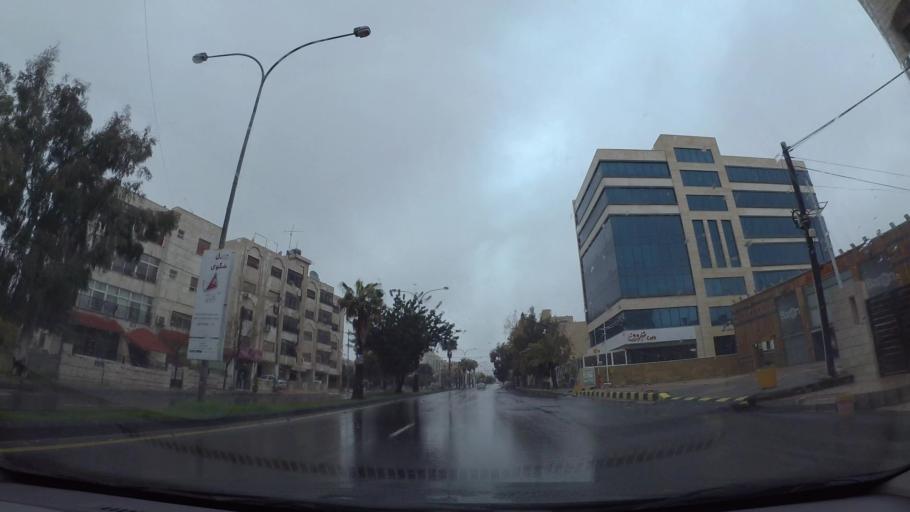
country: JO
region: Amman
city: Wadi as Sir
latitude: 31.9686
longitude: 35.8549
